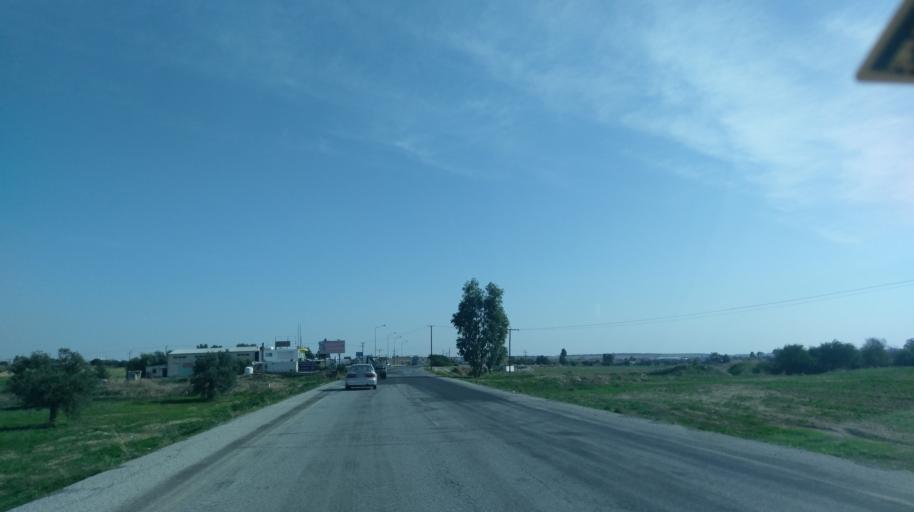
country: CY
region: Larnaka
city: Athienou
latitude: 35.2295
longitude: 33.5477
